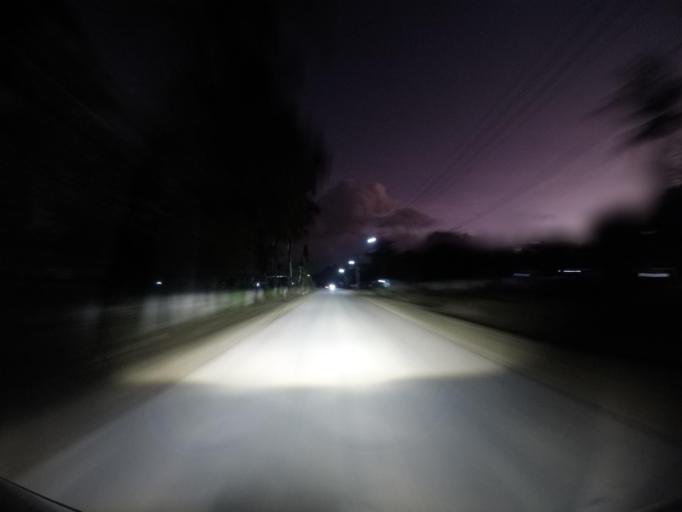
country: TL
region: Lautem
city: Lospalos
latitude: -8.4682
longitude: 126.9939
